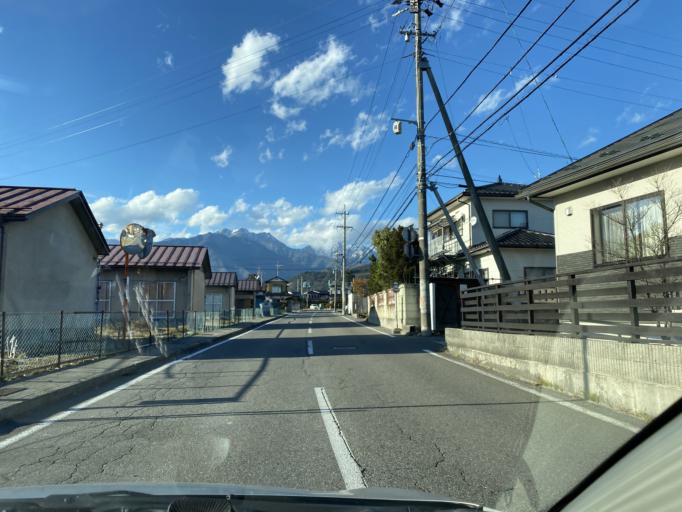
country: JP
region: Nagano
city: Omachi
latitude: 36.5178
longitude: 137.8413
